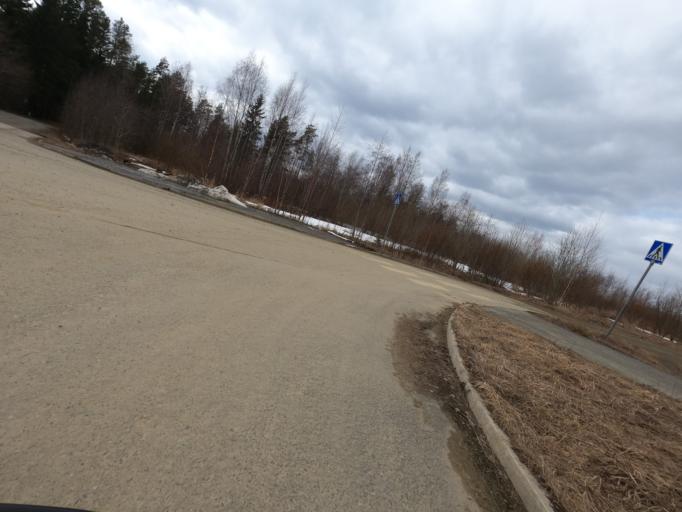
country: FI
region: North Karelia
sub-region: Joensuu
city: Joensuu
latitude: 62.5662
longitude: 29.7997
